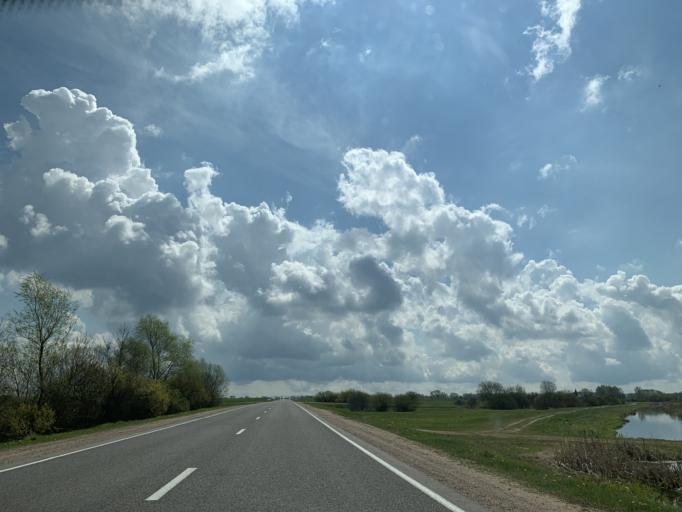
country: BY
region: Minsk
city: Nyasvizh
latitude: 53.2417
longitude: 26.7078
